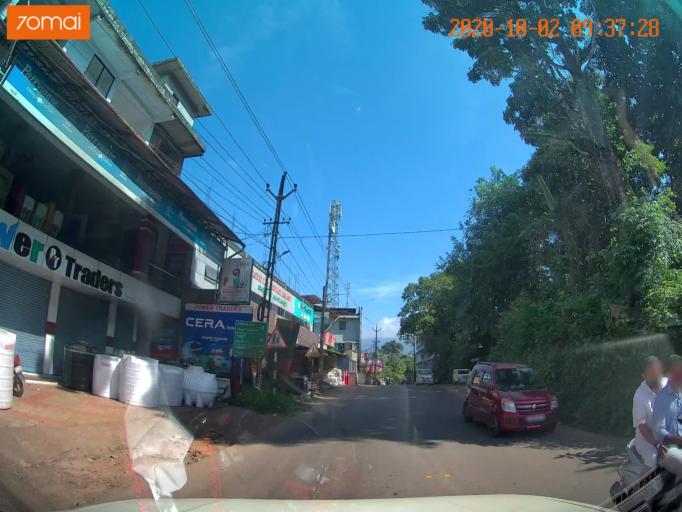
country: IN
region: Kerala
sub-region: Kozhikode
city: Nadapuram
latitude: 11.6521
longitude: 75.7535
